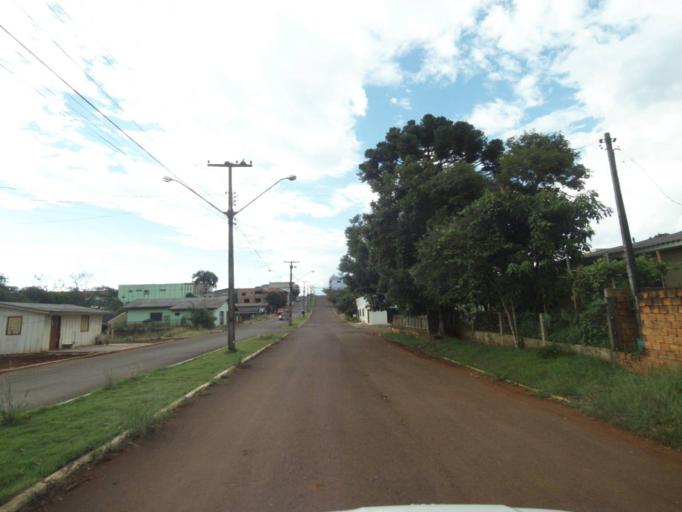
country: BR
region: Parana
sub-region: Laranjeiras Do Sul
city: Laranjeiras do Sul
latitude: -25.4940
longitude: -52.5279
